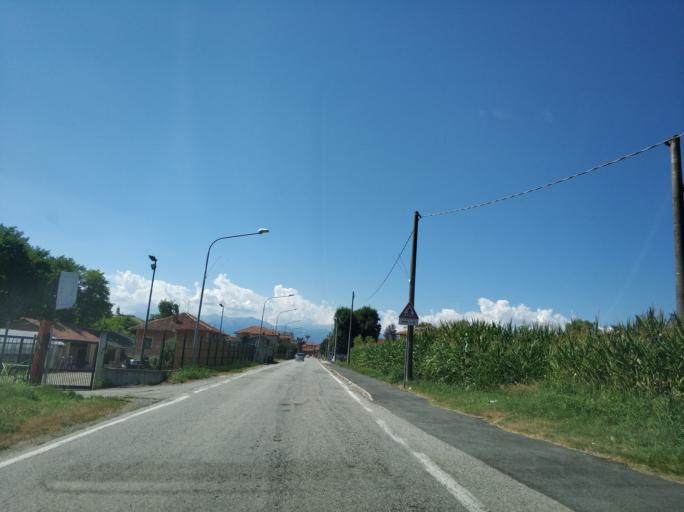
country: IT
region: Piedmont
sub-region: Provincia di Torino
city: San Benigno Canavese
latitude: 45.2194
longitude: 7.7914
